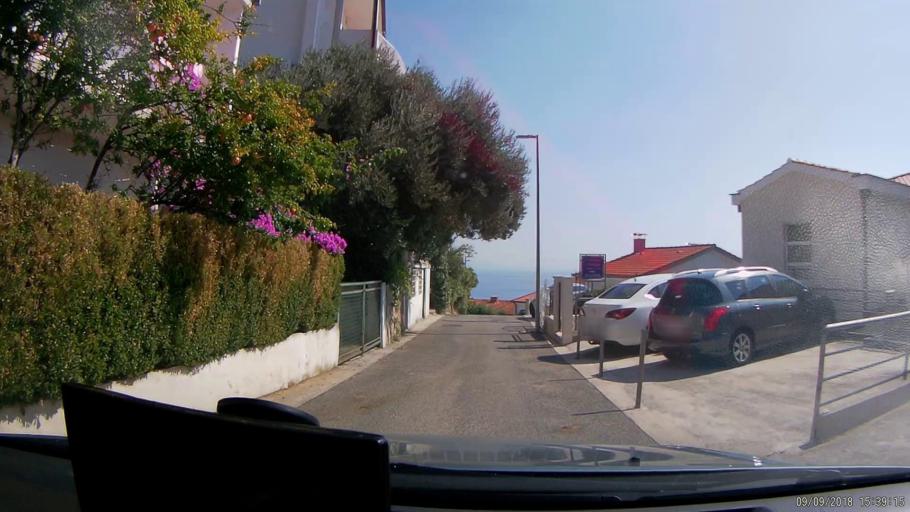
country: HR
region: Splitsko-Dalmatinska
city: Donja Brela
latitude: 43.3692
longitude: 16.9315
